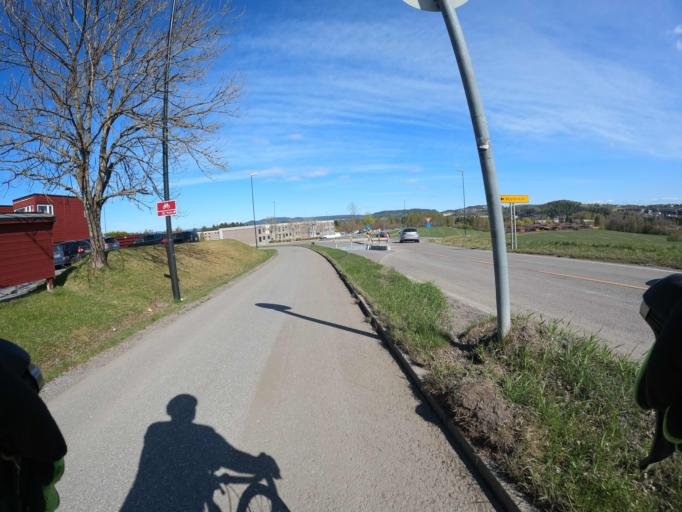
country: NO
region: Akershus
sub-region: Skedsmo
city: Lillestrom
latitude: 59.9674
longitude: 11.0075
